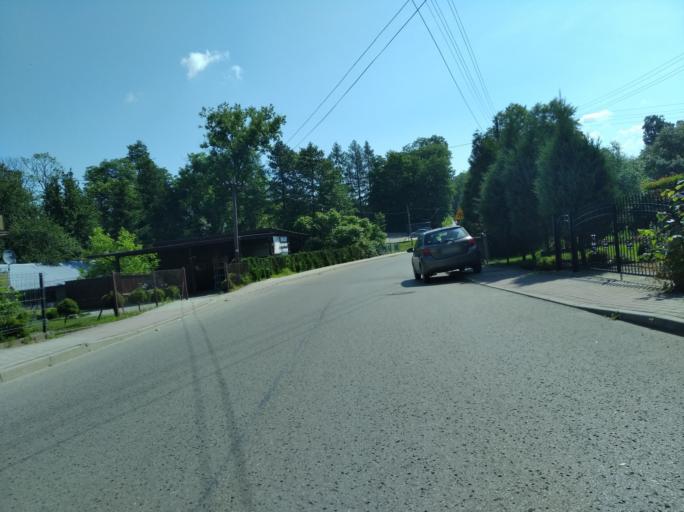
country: PL
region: Subcarpathian Voivodeship
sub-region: Powiat rzeszowski
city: Dynow
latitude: 49.8141
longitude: 22.2258
